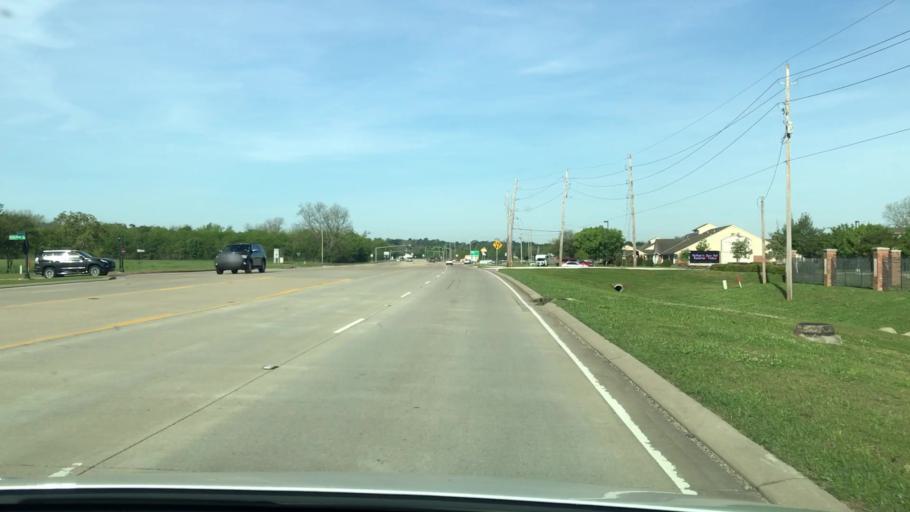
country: US
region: Louisiana
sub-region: Bossier Parish
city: Bossier City
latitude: 32.4011
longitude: -93.7101
